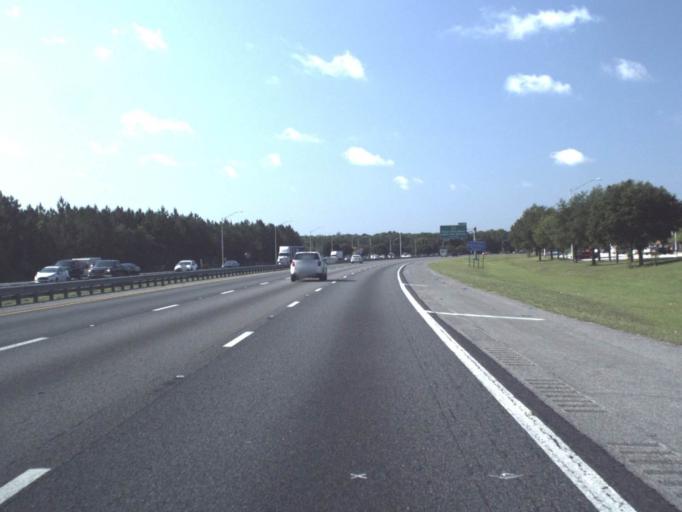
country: US
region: Florida
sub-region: Saint Johns County
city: Palm Valley
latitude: 30.0969
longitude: -81.4991
